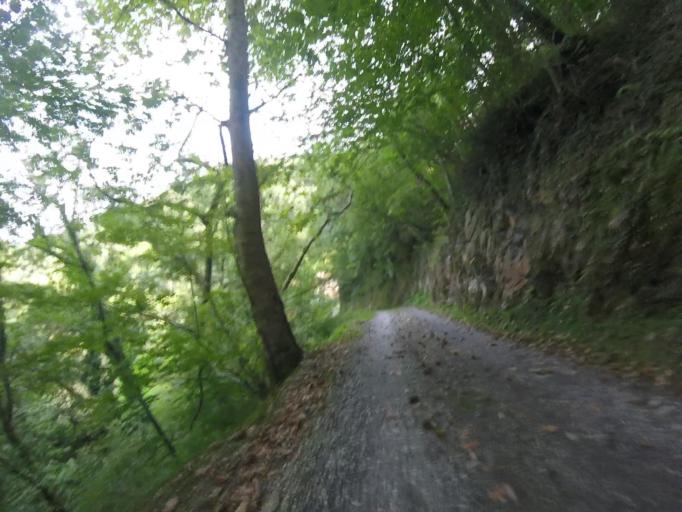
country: ES
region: Navarre
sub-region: Provincia de Navarra
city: Arano
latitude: 43.2238
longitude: -1.9305
